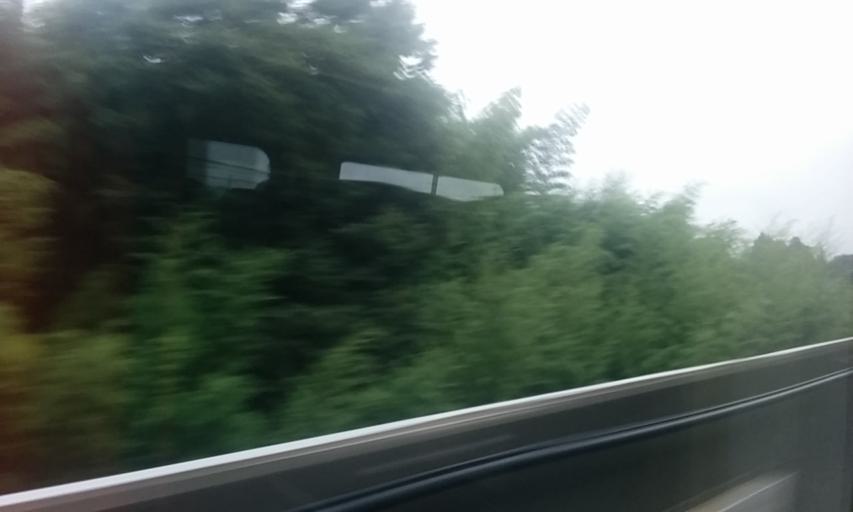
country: JP
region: Tochigi
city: Otawara
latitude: 36.9130
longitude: 140.0069
